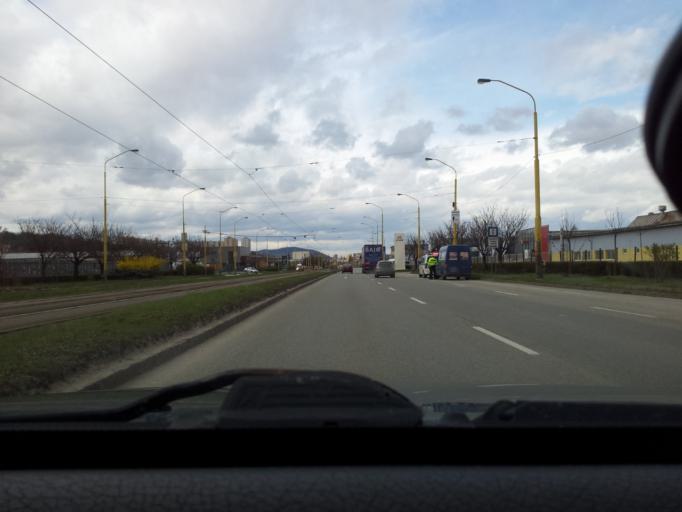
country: SK
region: Kosicky
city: Kosice
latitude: 48.6911
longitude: 21.2656
